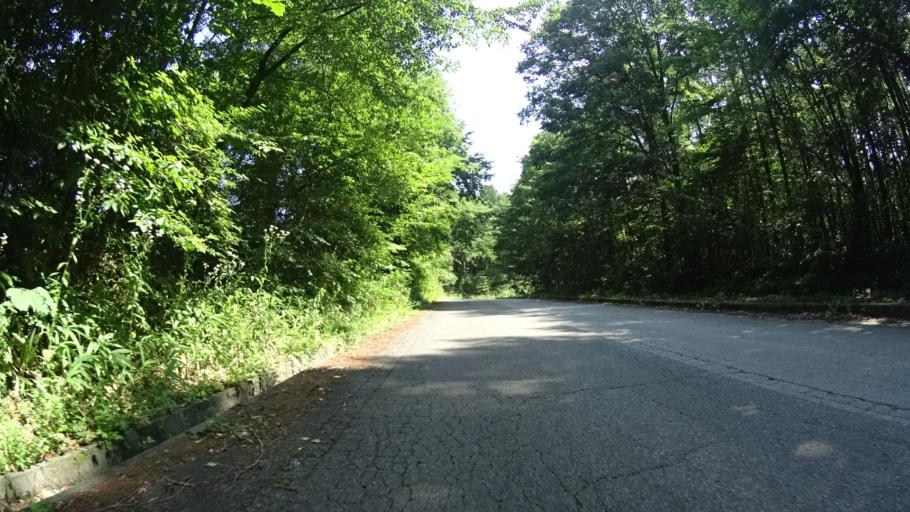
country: JP
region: Yamanashi
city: Nirasaki
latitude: 35.9105
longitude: 138.4288
